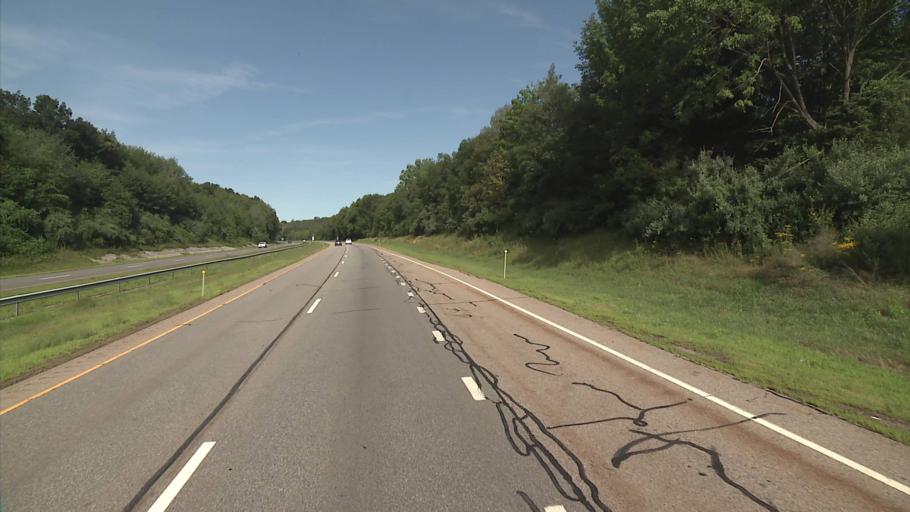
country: US
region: Connecticut
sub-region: New London County
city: Montville Center
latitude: 41.5712
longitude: -72.1862
